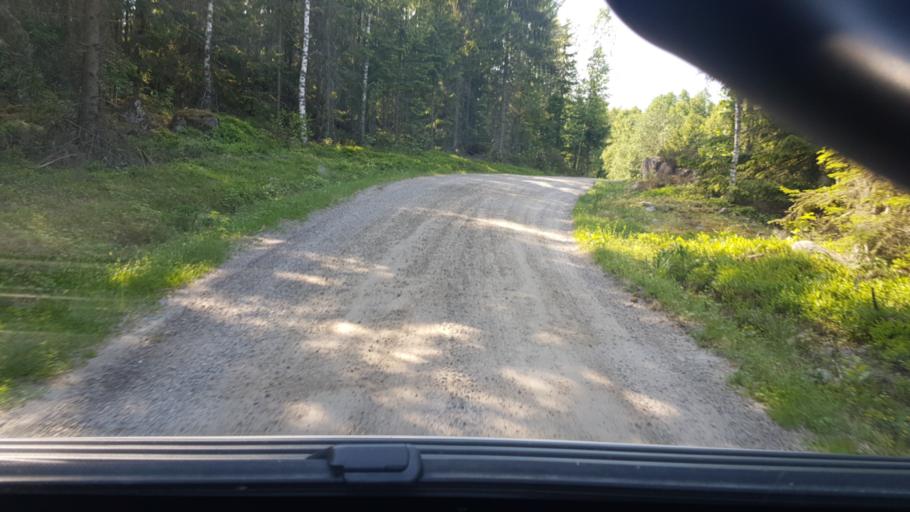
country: SE
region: Vaermland
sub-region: Eda Kommun
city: Amotfors
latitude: 59.8242
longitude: 12.4070
